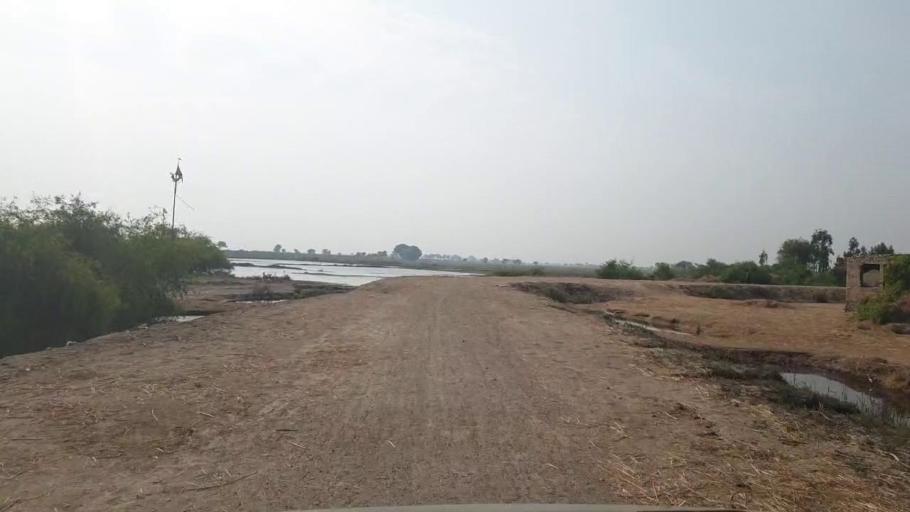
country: PK
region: Sindh
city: Tando Muhammad Khan
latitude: 25.1077
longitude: 68.4930
